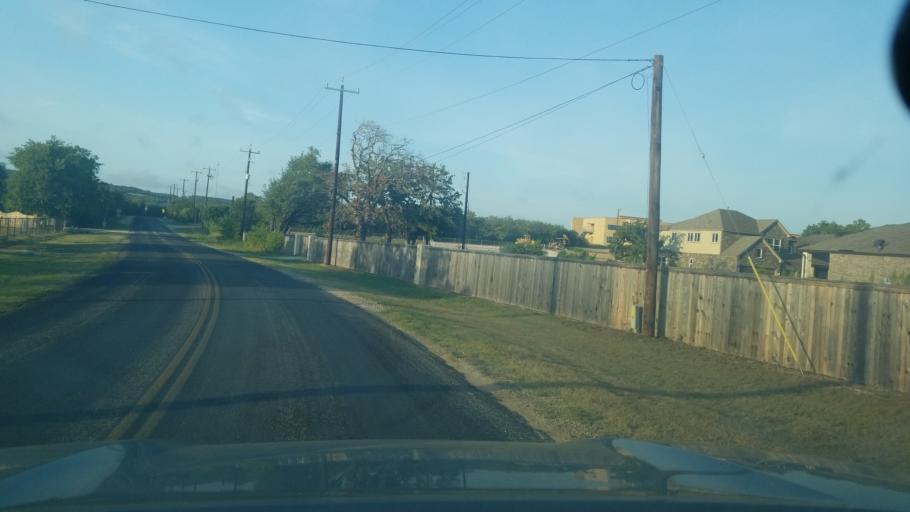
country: US
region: Texas
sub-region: Comal County
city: Bulverde
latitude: 29.7276
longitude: -98.4534
